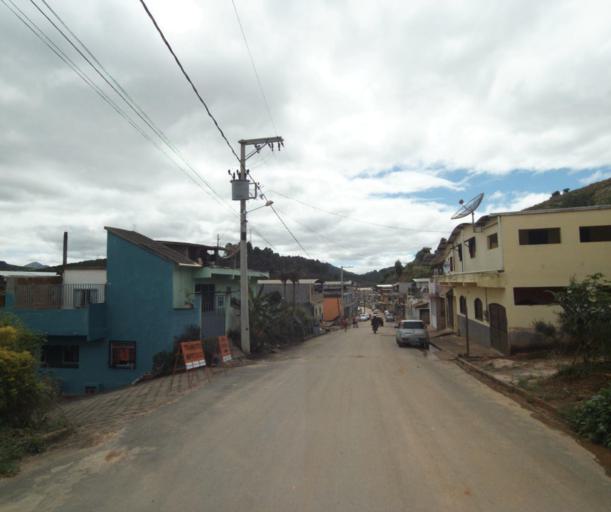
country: BR
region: Espirito Santo
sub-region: Irupi
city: Irupi
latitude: -20.3506
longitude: -41.6473
